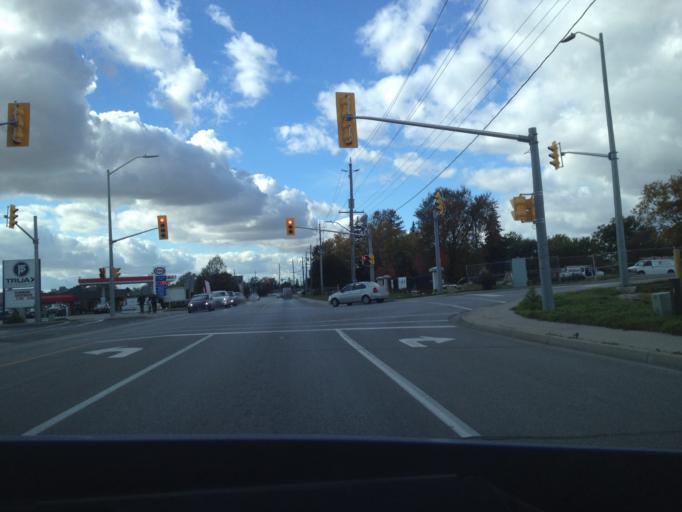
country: CA
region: Ontario
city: Amherstburg
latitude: 42.0378
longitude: -82.7222
